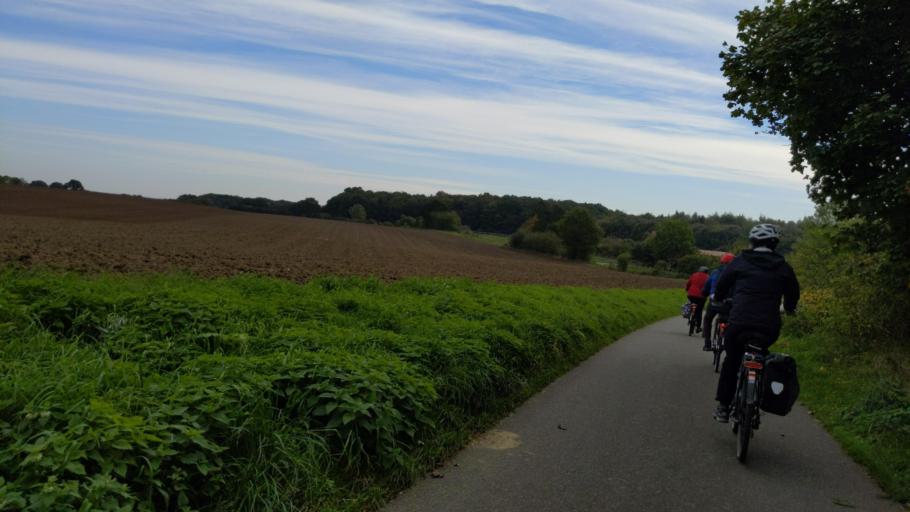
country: DE
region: Schleswig-Holstein
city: Rehhorst
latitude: 53.8696
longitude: 10.4766
